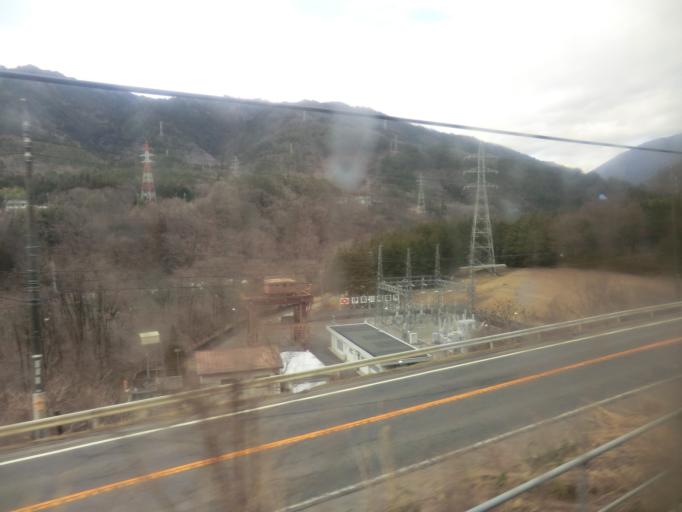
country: JP
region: Nagano
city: Iida
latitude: 35.7038
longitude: 137.6997
